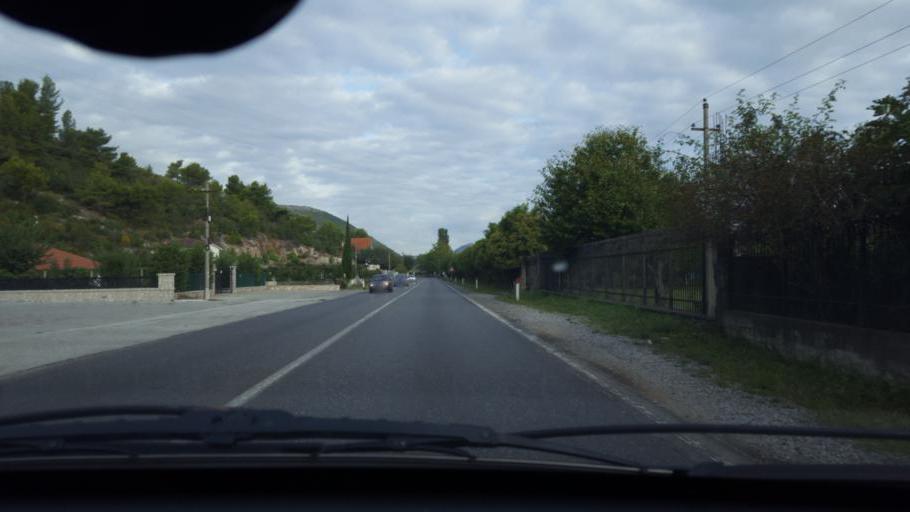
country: AL
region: Lezhe
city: Lezhe
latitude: 41.7924
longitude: 19.6381
